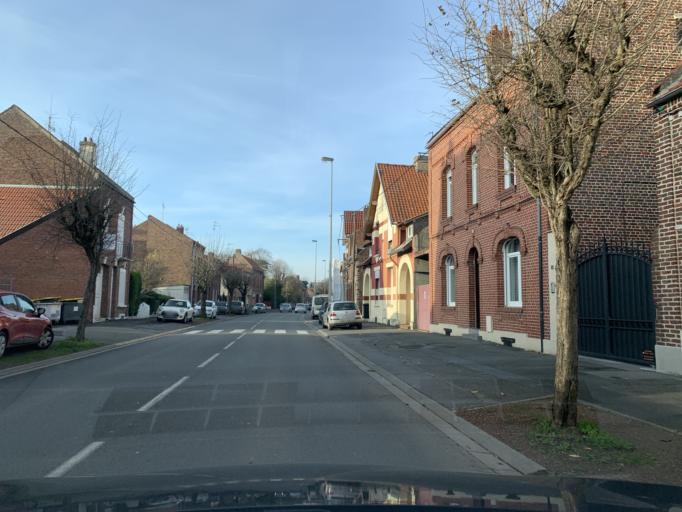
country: FR
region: Nord-Pas-de-Calais
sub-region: Departement du Nord
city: Cambrai
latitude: 50.1649
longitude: 3.2441
